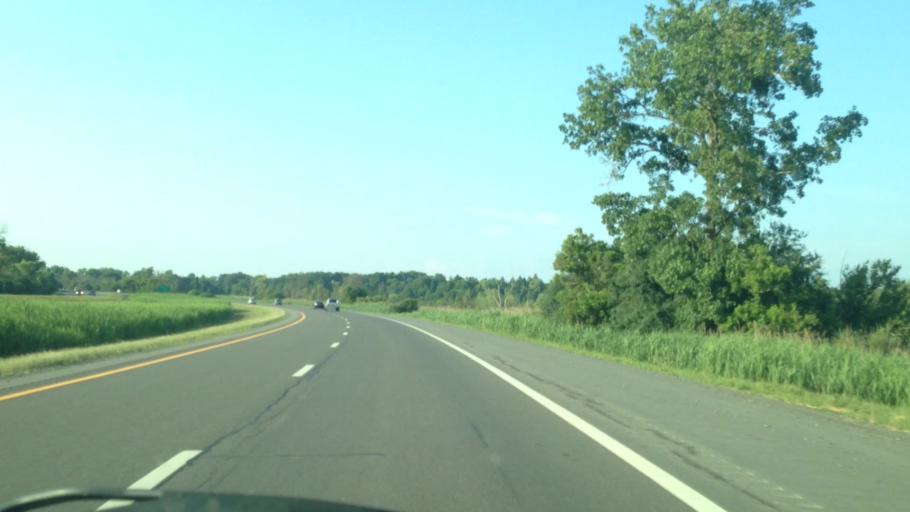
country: US
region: New York
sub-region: Onondaga County
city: East Syracuse
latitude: 43.0193
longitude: -76.0633
